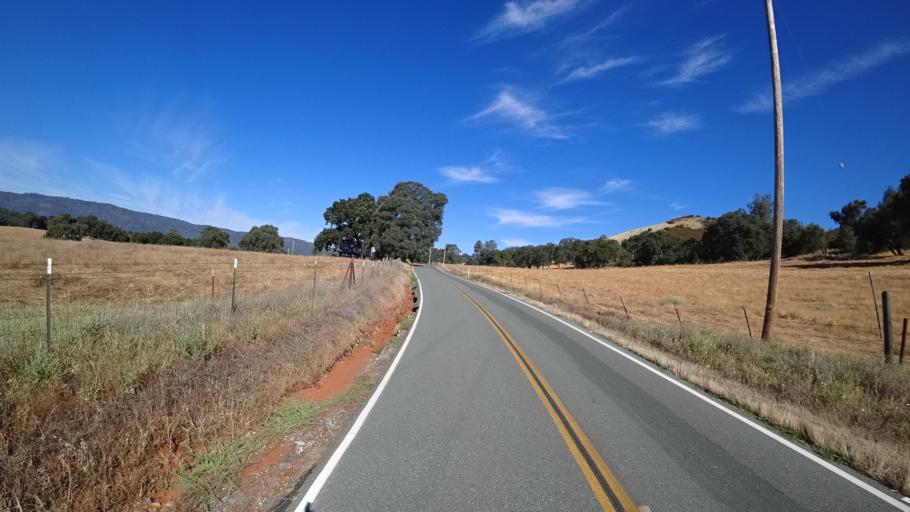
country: US
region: California
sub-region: Calaveras County
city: San Andreas
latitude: 38.1712
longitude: -120.6309
